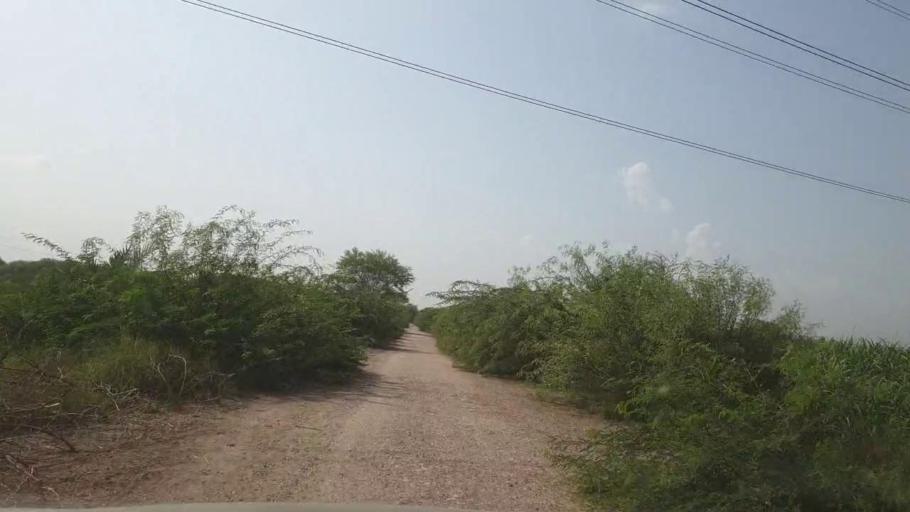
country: PK
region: Sindh
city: Pano Aqil
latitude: 27.7691
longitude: 69.1674
